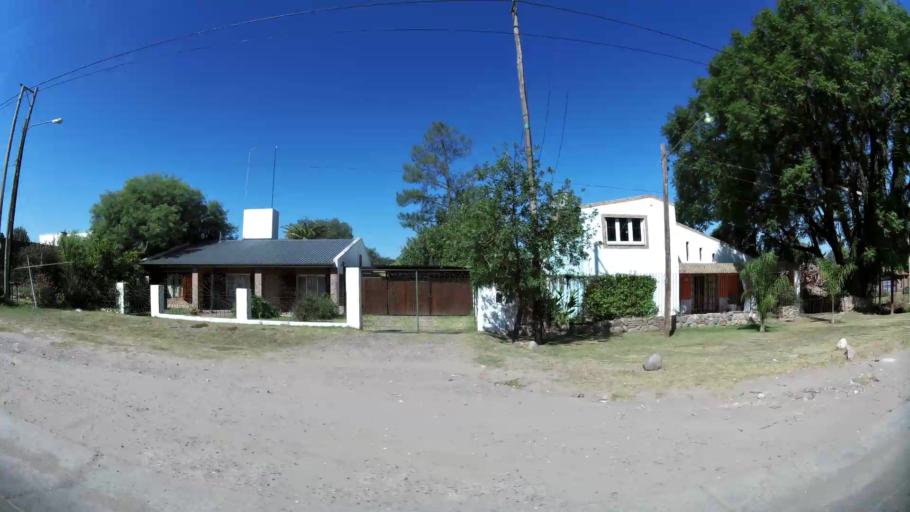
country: AR
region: Cordoba
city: Saldan
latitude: -31.3177
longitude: -64.2883
